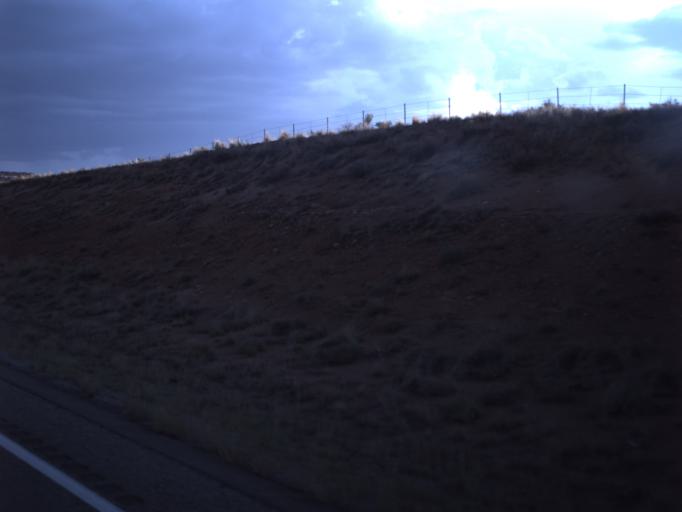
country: US
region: Utah
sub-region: San Juan County
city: Monticello
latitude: 38.1198
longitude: -109.3664
